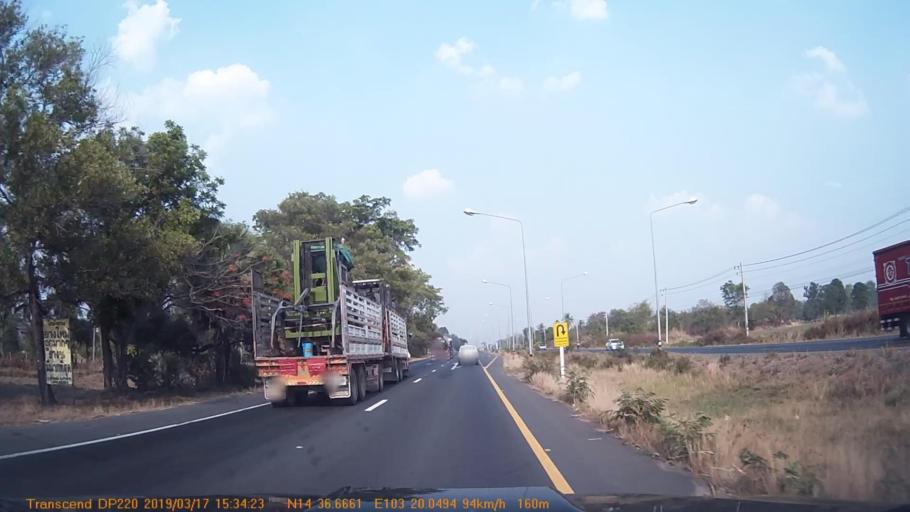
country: TH
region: Surin
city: Prasat
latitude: 14.6112
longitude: 103.3346
